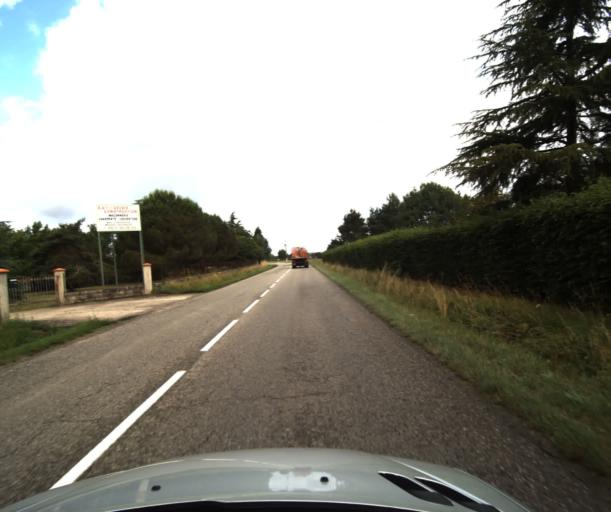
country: FR
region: Midi-Pyrenees
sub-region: Departement du Tarn-et-Garonne
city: Castelsarrasin
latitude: 44.0278
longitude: 1.0577
